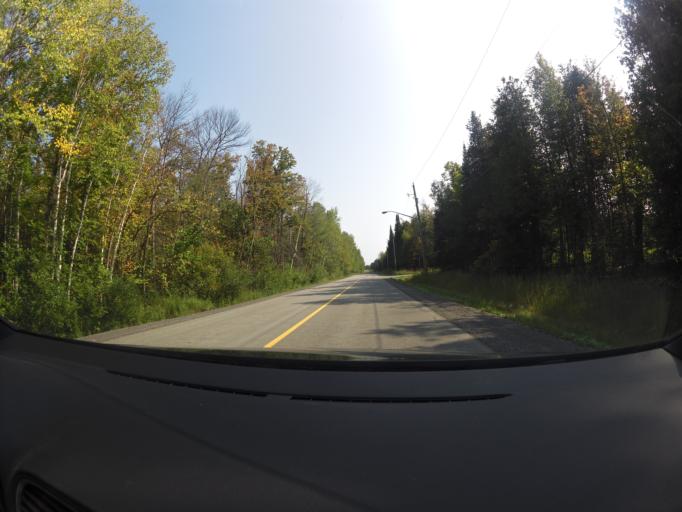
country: CA
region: Ontario
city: Carleton Place
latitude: 45.3286
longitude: -76.1547
